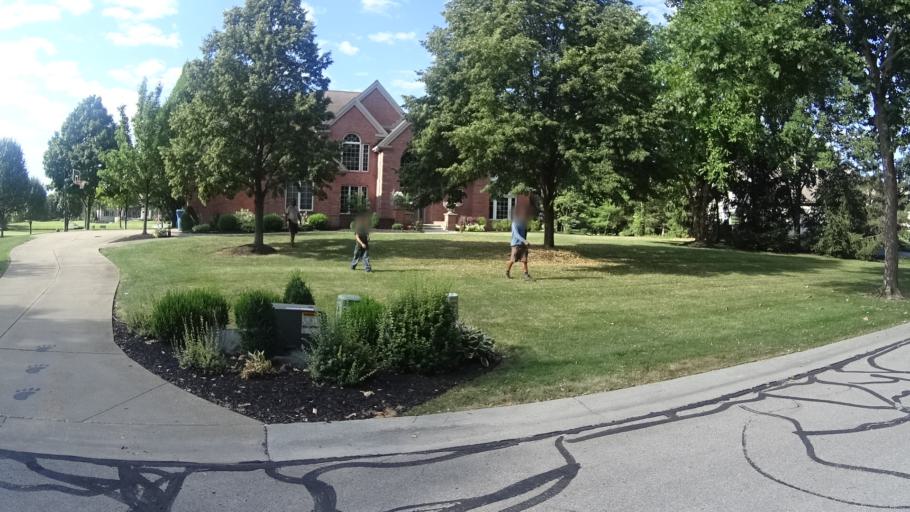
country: US
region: Ohio
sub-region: Erie County
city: Sandusky
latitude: 41.4169
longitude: -82.6567
